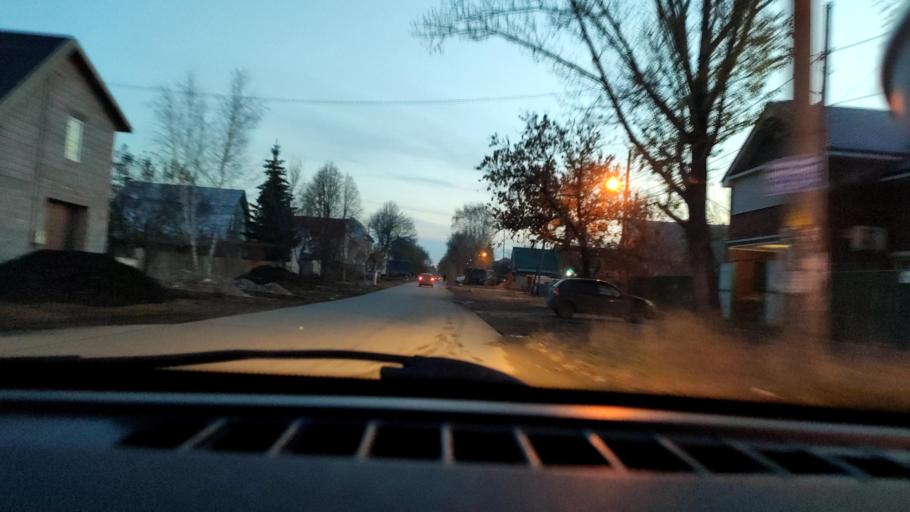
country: RU
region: Samara
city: Petra-Dubrava
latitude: 53.2602
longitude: 50.3298
